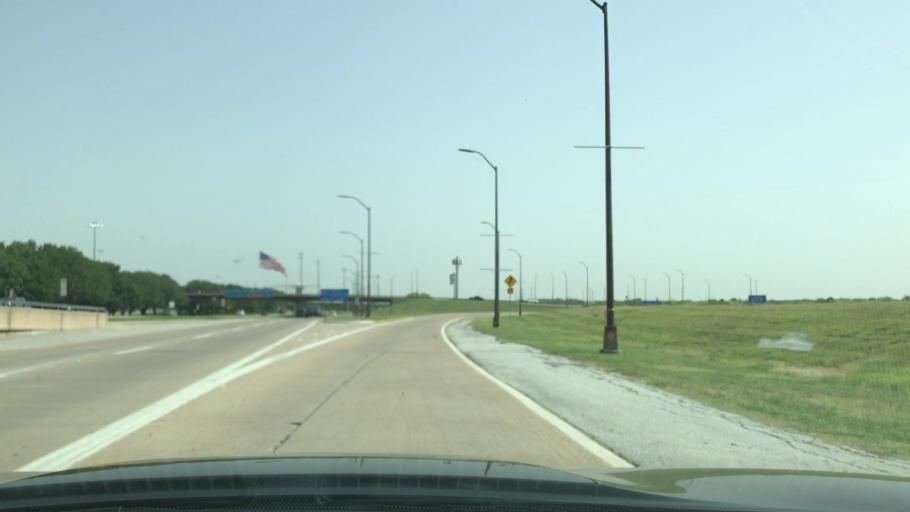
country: US
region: Texas
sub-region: Tarrant County
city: Euless
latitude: 32.8591
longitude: -97.0400
